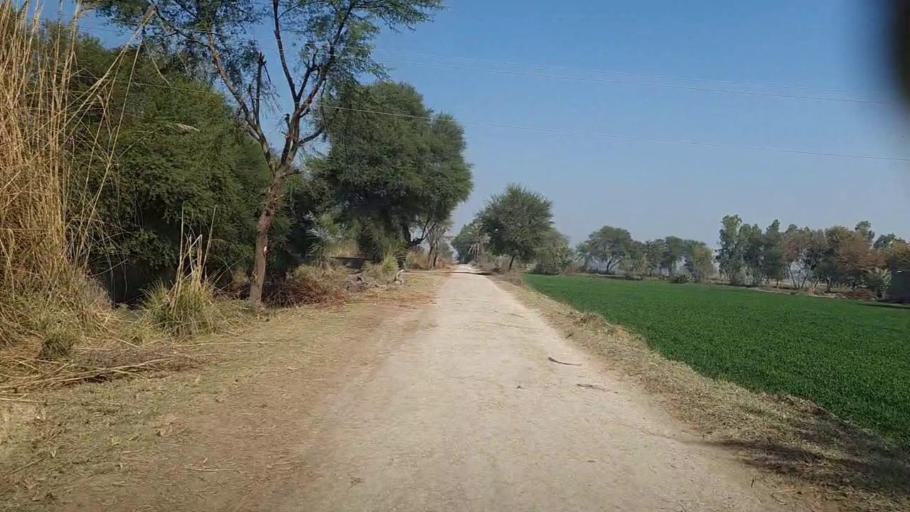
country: PK
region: Sindh
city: Khairpur
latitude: 27.9766
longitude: 69.7101
